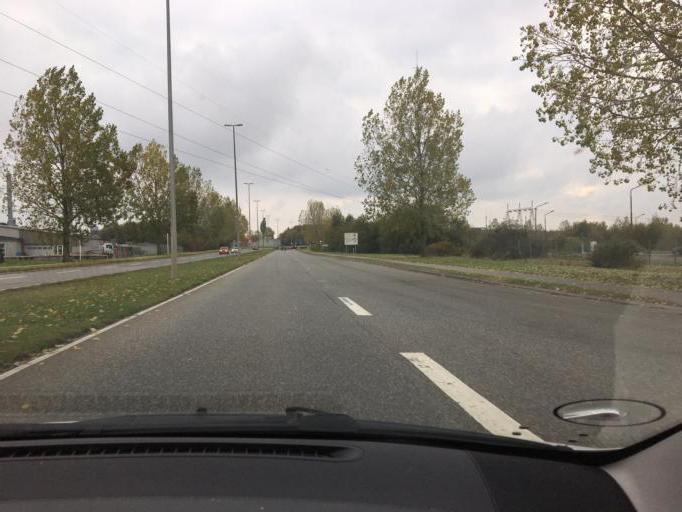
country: DK
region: South Denmark
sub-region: Fredericia Kommune
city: Fredericia
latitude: 55.5912
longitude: 9.7547
